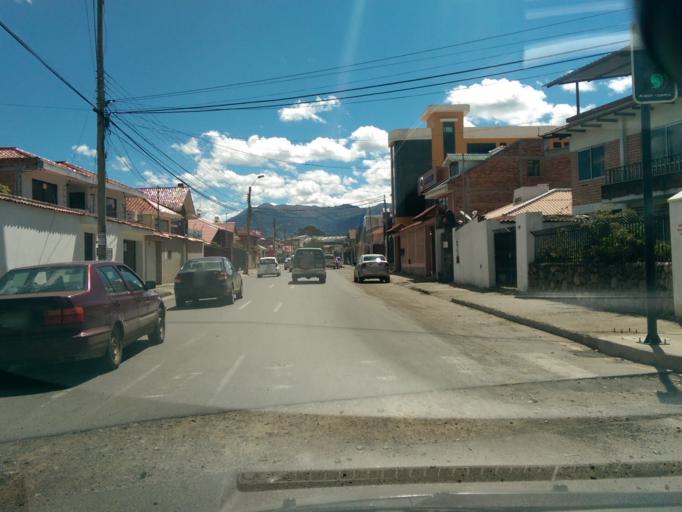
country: EC
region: Azuay
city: Cuenca
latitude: -2.9031
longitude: -79.0126
